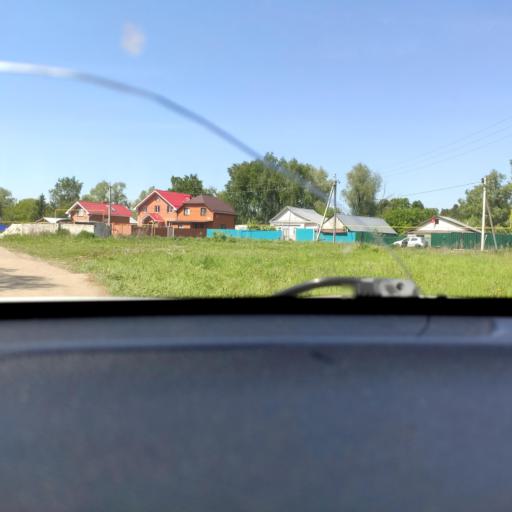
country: RU
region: Tatarstan
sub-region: Gorod Kazan'
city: Kazan
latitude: 55.8637
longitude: 49.1962
